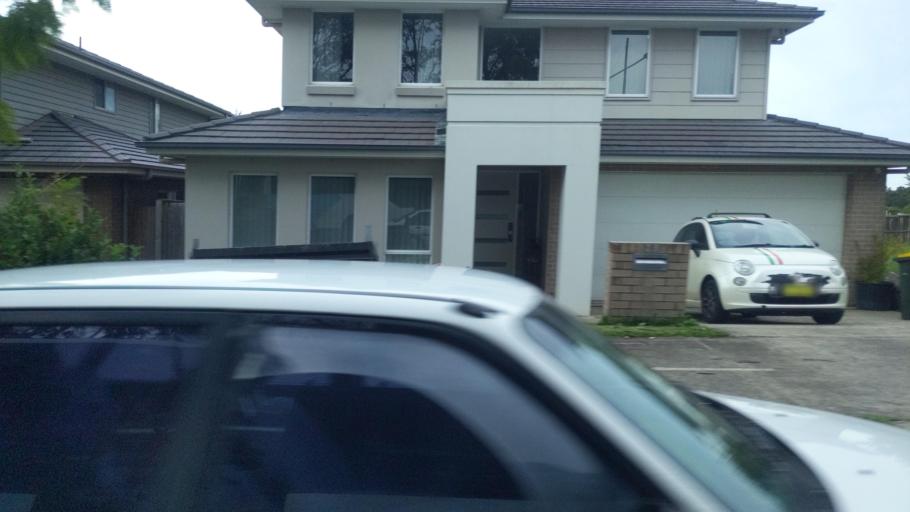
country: AU
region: New South Wales
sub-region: Blacktown
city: Quakers Hill
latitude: -33.7289
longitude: 150.8657
